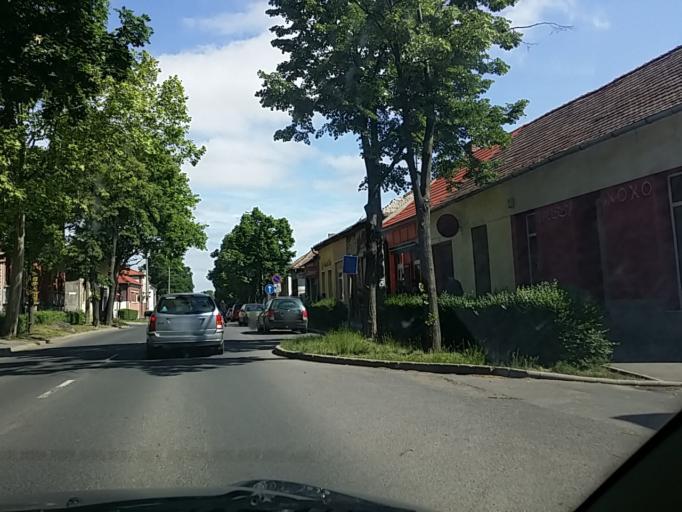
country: HU
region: Borsod-Abauj-Zemplen
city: Satoraljaujhely
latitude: 48.3917
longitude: 21.6562
